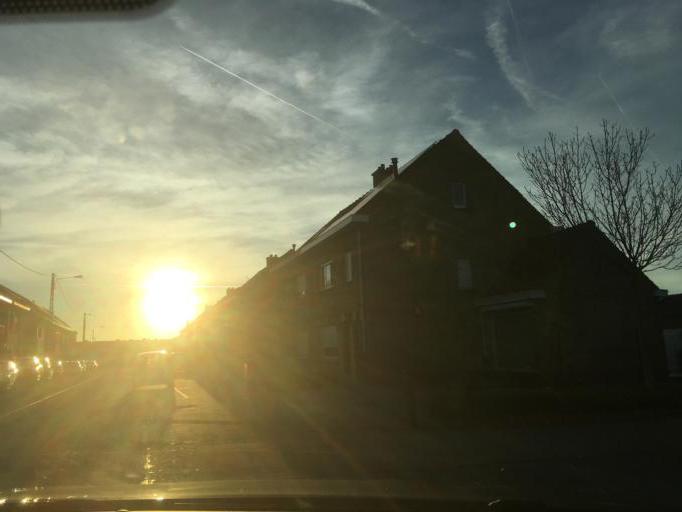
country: BE
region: Flanders
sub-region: Provincie West-Vlaanderen
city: Meulebeke
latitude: 50.9523
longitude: 3.2819
